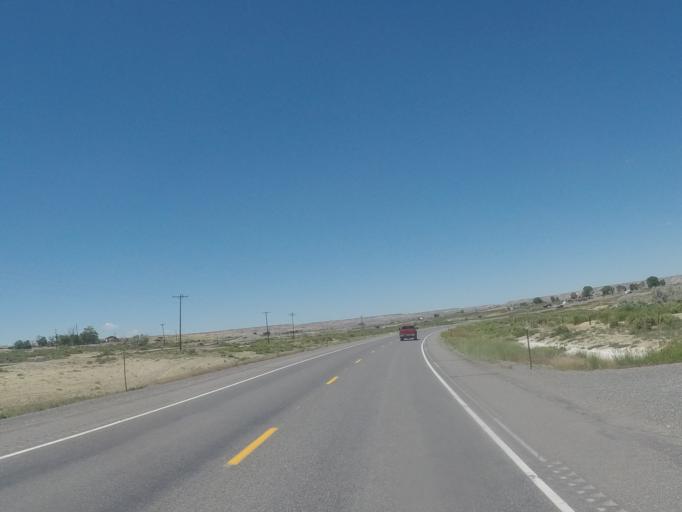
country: US
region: Wyoming
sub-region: Park County
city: Powell
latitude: 44.9173
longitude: -108.6173
